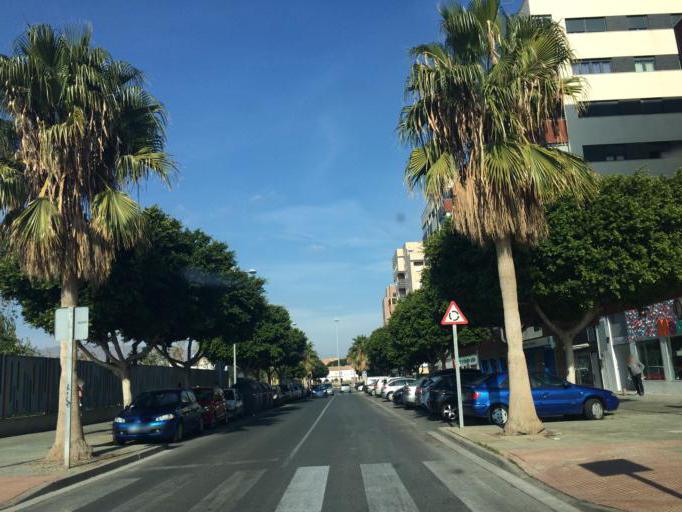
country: ES
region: Andalusia
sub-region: Provincia de Almeria
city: Almeria
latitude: 36.8298
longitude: -2.4436
